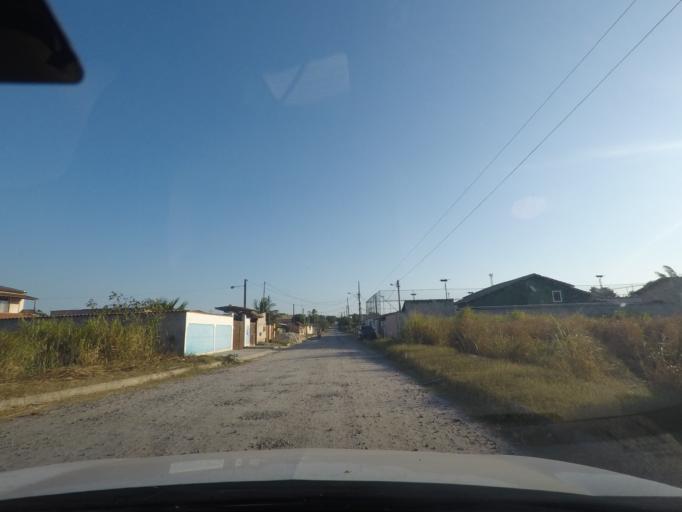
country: BR
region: Rio de Janeiro
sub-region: Marica
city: Marica
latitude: -22.9649
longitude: -42.9325
